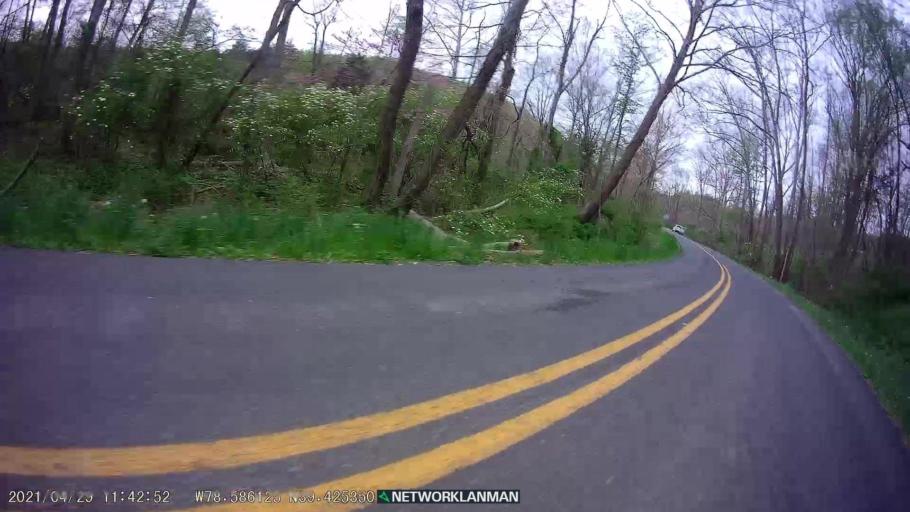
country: US
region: West Virginia
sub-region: Hampshire County
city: Romney
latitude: 39.4256
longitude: -78.5864
